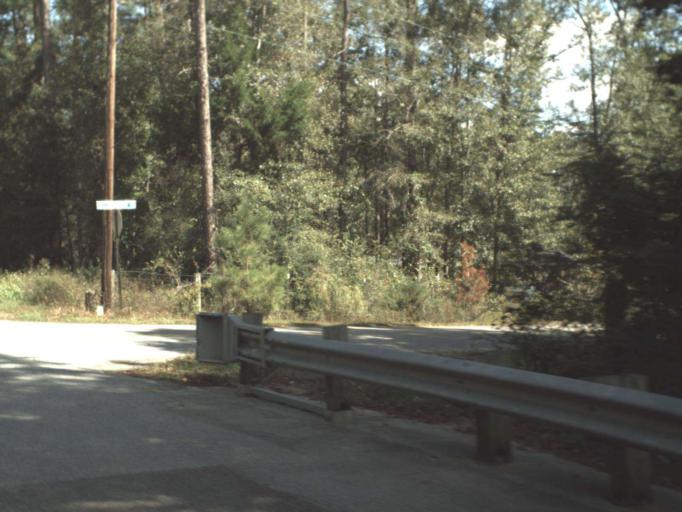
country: US
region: Alabama
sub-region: Geneva County
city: Samson
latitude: 30.9685
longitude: -86.1359
